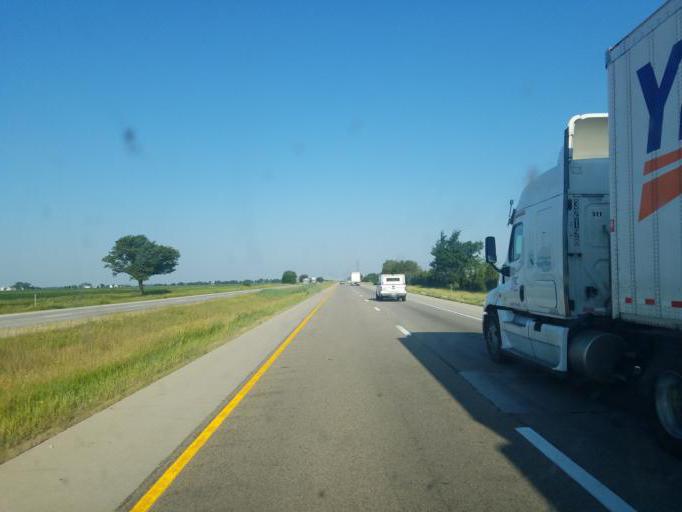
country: US
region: Illinois
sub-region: Grundy County
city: Morris
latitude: 41.3776
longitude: -88.5256
